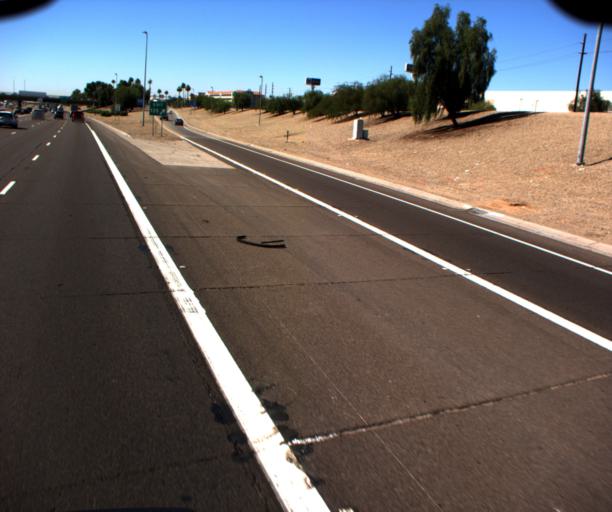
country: US
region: Arizona
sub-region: Maricopa County
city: Glendale
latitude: 33.4629
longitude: -112.1647
